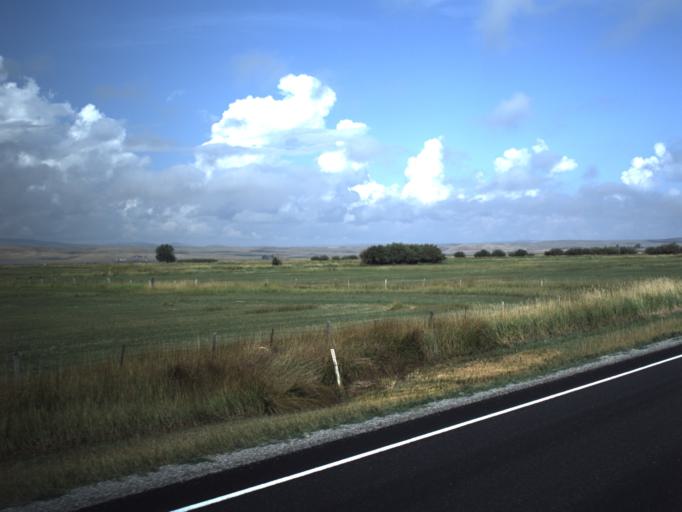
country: US
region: Utah
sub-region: Rich County
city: Randolph
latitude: 41.6317
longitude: -111.1790
